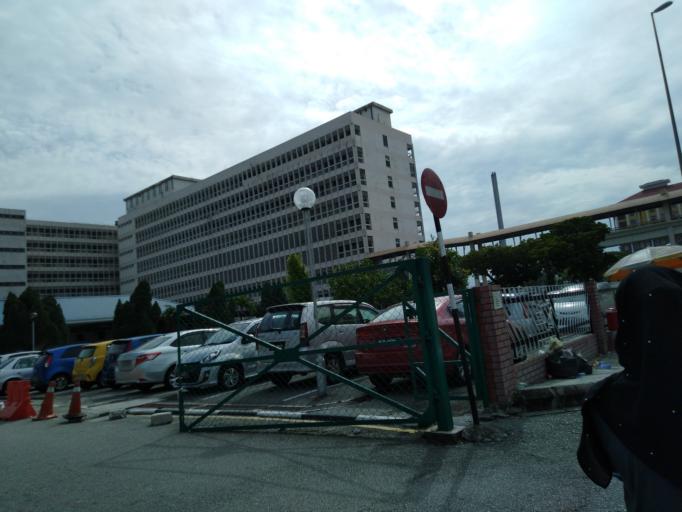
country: MY
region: Perak
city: Ipoh
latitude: 4.6025
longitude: 101.0903
